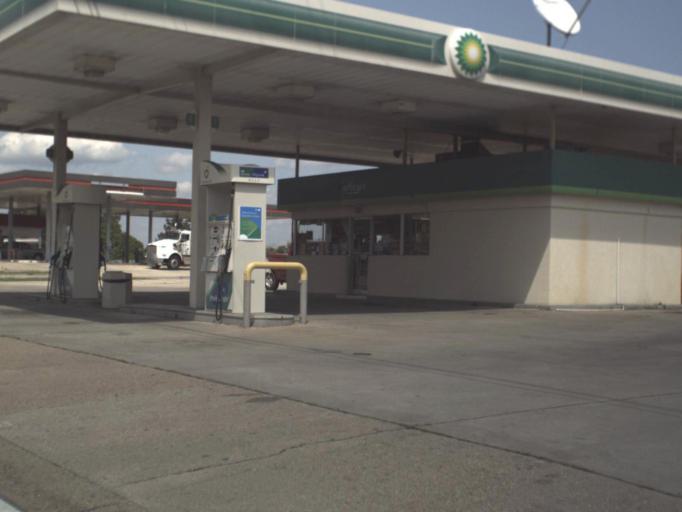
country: US
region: Florida
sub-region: Escambia County
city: Century
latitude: 30.9809
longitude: -87.2579
